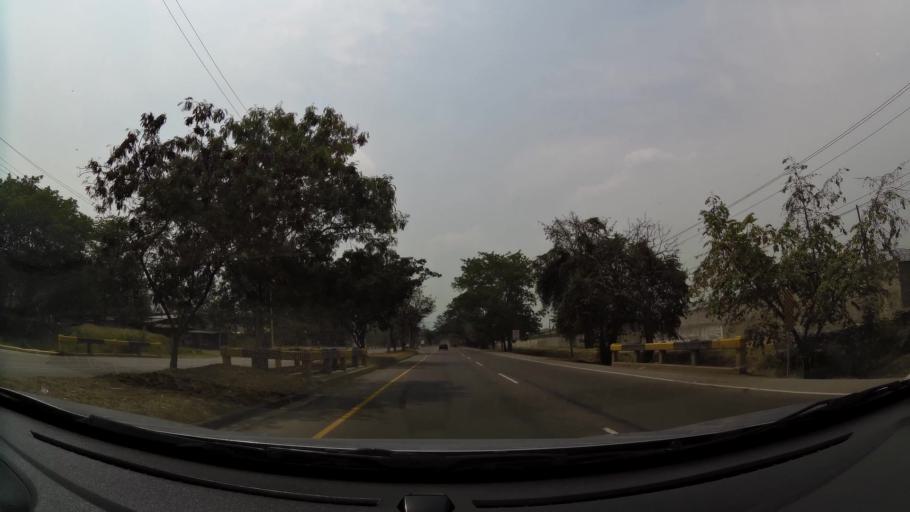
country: HN
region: Cortes
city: Chotepe
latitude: 15.3944
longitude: -87.9943
